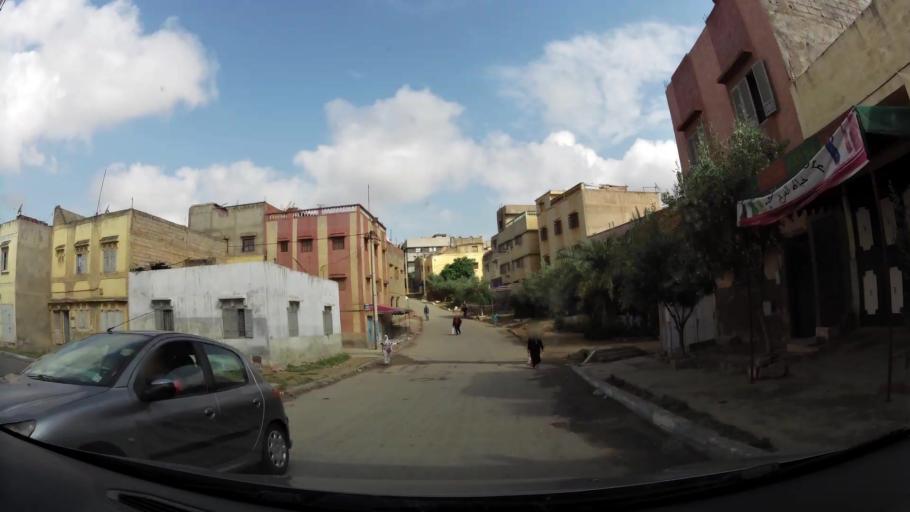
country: MA
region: Rabat-Sale-Zemmour-Zaer
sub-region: Khemisset
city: Tiflet
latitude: 33.8948
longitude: -6.3155
